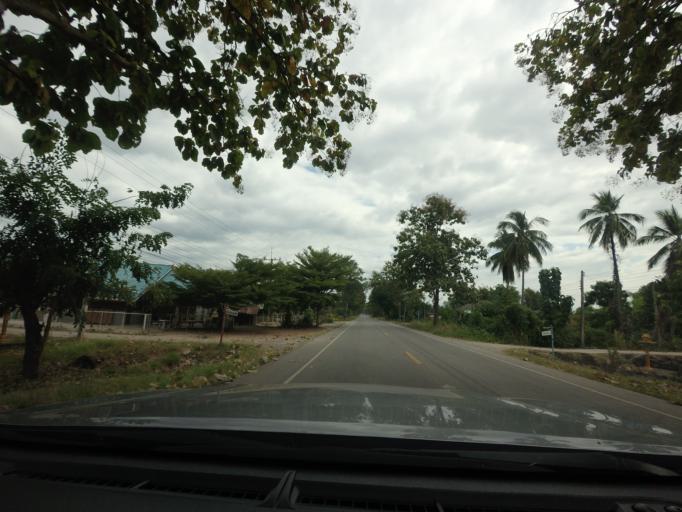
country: TH
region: Phitsanulok
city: Wang Thong
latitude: 16.7105
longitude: 100.4815
